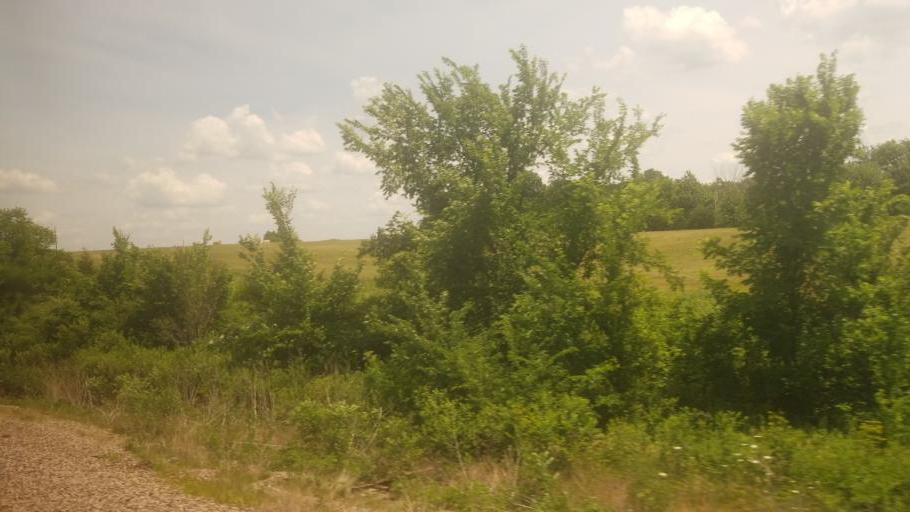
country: US
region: Missouri
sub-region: Macon County
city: La Plata
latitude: 40.0808
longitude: -92.4317
